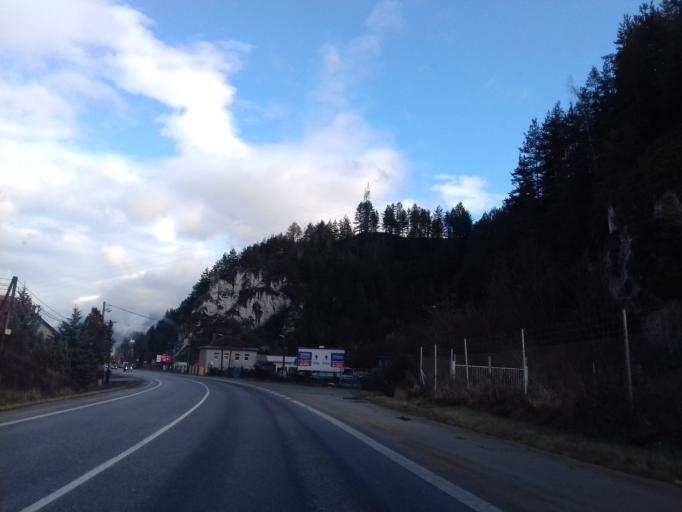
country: SK
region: Zilinsky
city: Ruzomberok
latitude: 49.0572
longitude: 19.3061
